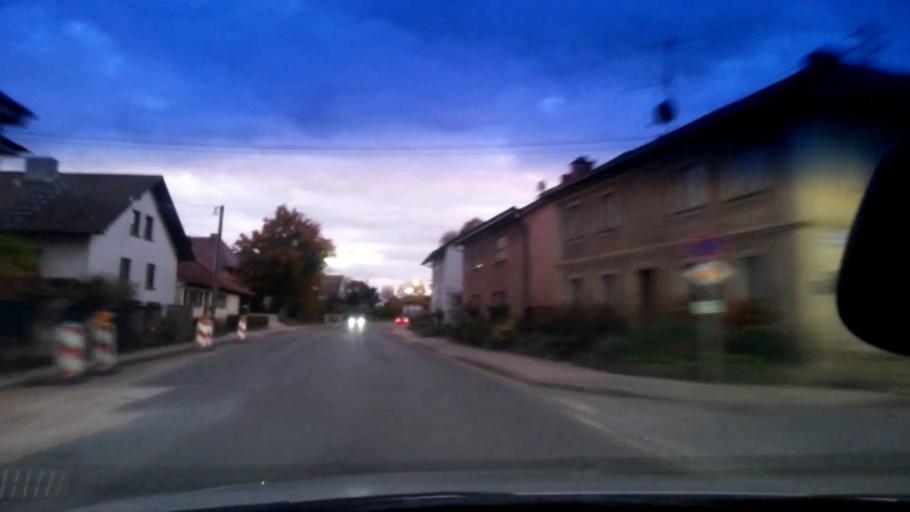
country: DE
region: Bavaria
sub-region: Upper Franconia
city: Schesslitz
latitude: 49.9748
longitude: 11.0295
